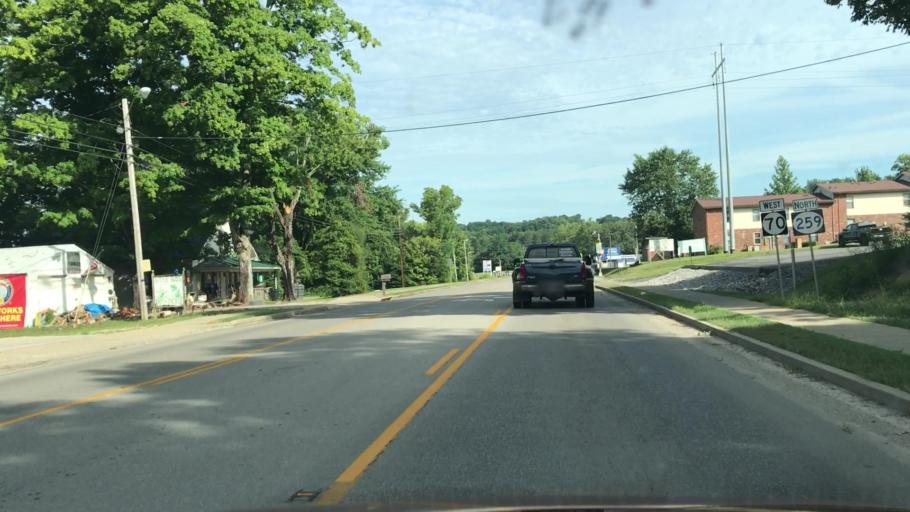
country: US
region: Kentucky
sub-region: Edmonson County
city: Brownsville
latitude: 37.1880
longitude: -86.2528
